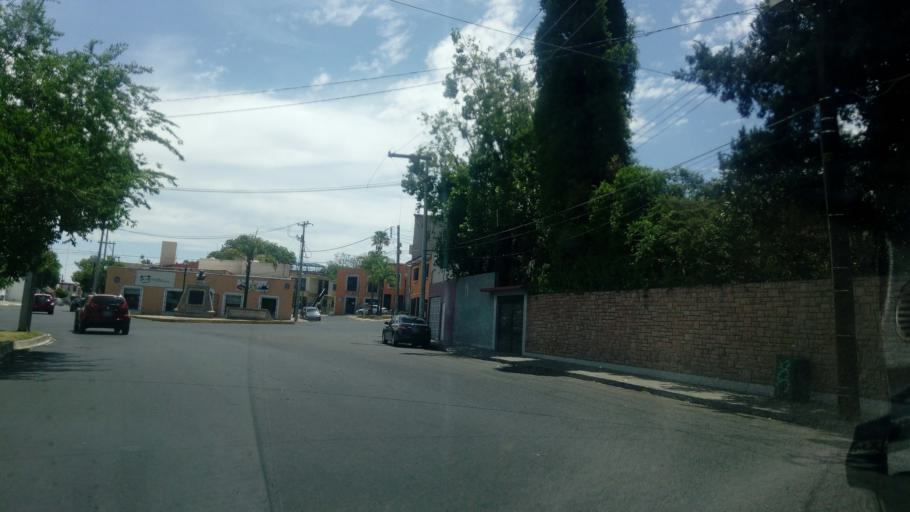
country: MX
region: Durango
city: Victoria de Durango
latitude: 24.0249
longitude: -104.6772
